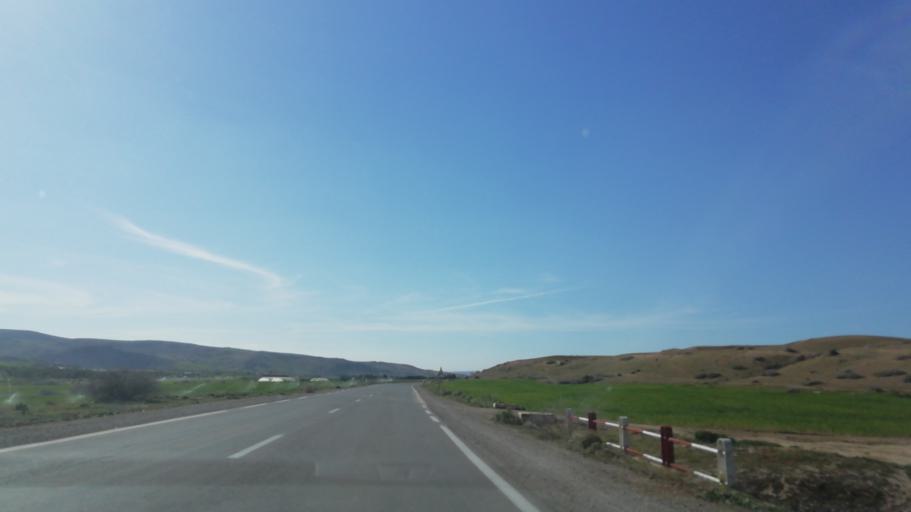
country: DZ
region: Mascara
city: Oued el Abtal
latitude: 35.4497
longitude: 0.7936
